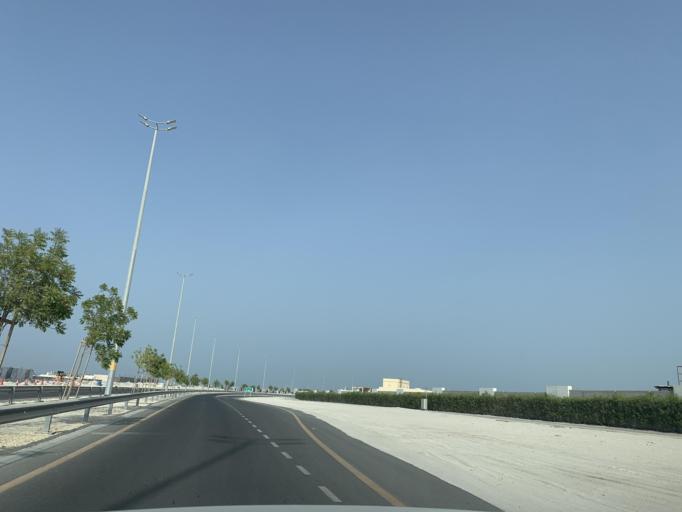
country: BH
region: Muharraq
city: Al Muharraq
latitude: 26.3126
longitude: 50.6369
